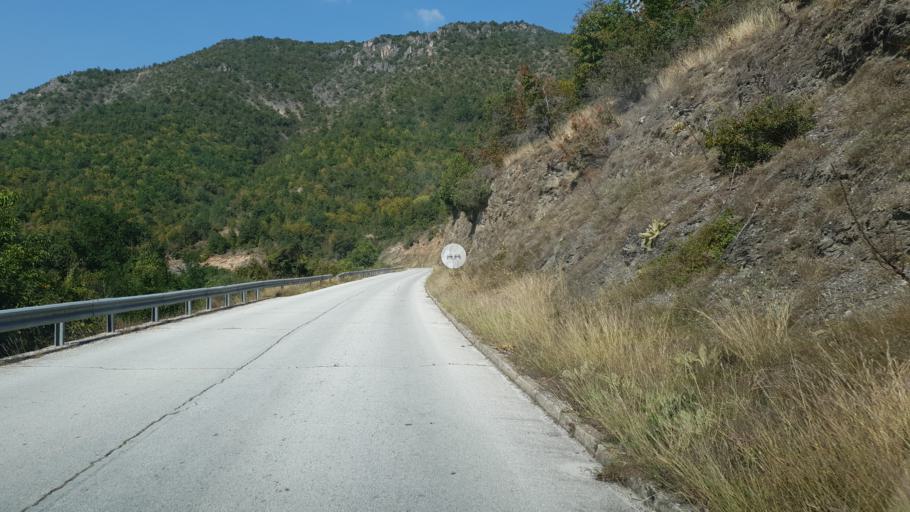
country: MK
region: Makedonski Brod
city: Samokov
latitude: 41.6694
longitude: 21.2432
